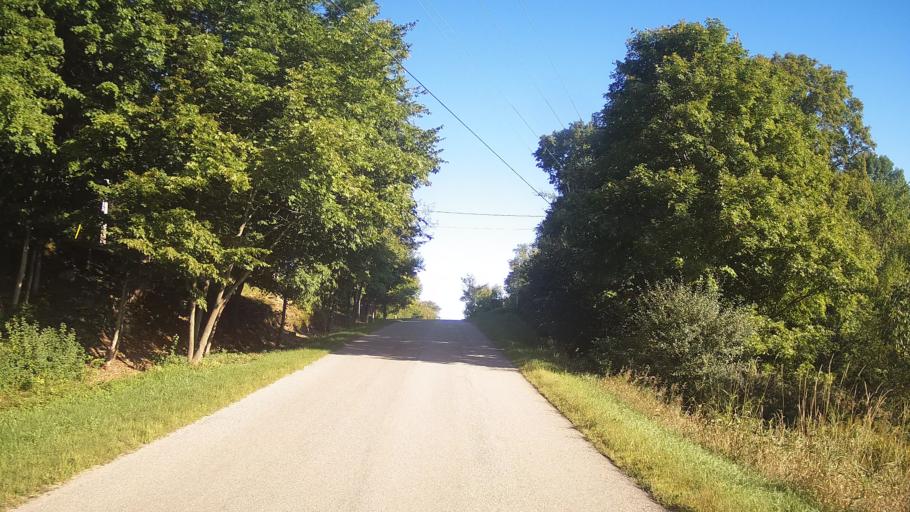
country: US
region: New York
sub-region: Jefferson County
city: Alexandria Bay
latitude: 44.4481
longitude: -75.9847
